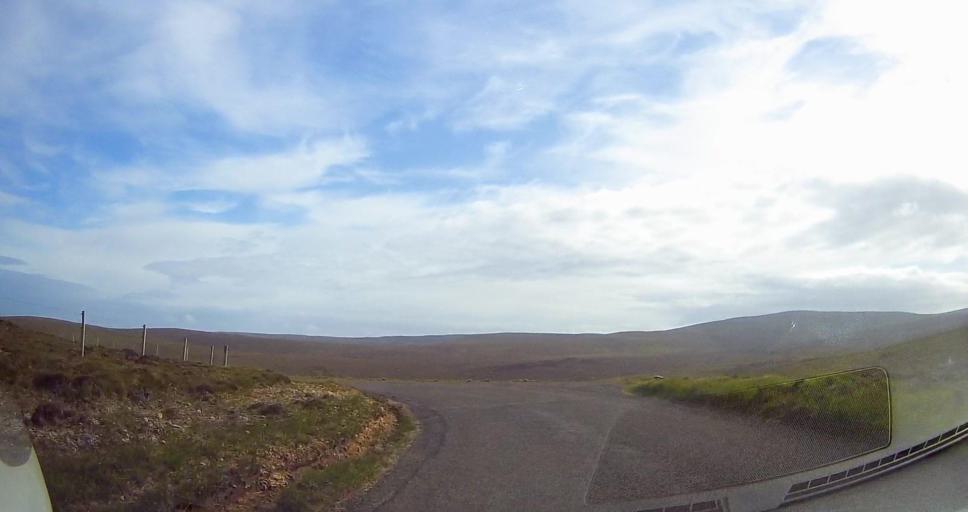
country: GB
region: Scotland
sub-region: Orkney Islands
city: Stromness
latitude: 58.8797
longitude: -3.2487
